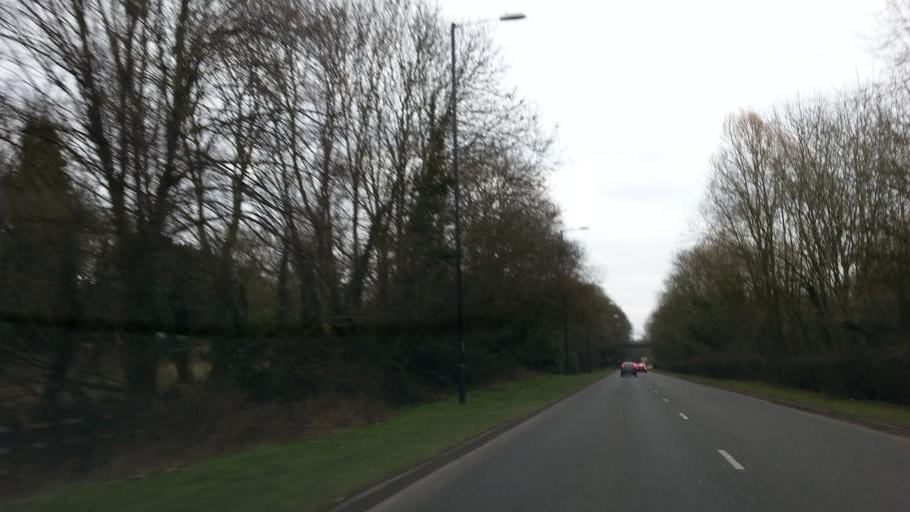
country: GB
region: England
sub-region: Coventry
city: Keresley
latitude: 52.4223
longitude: -1.5622
